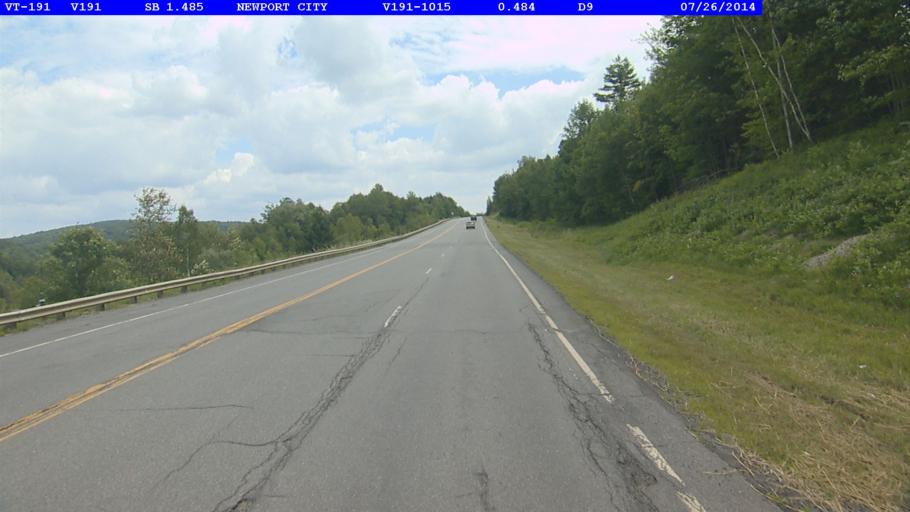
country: US
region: Vermont
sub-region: Orleans County
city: Newport
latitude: 44.9368
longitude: -72.1894
